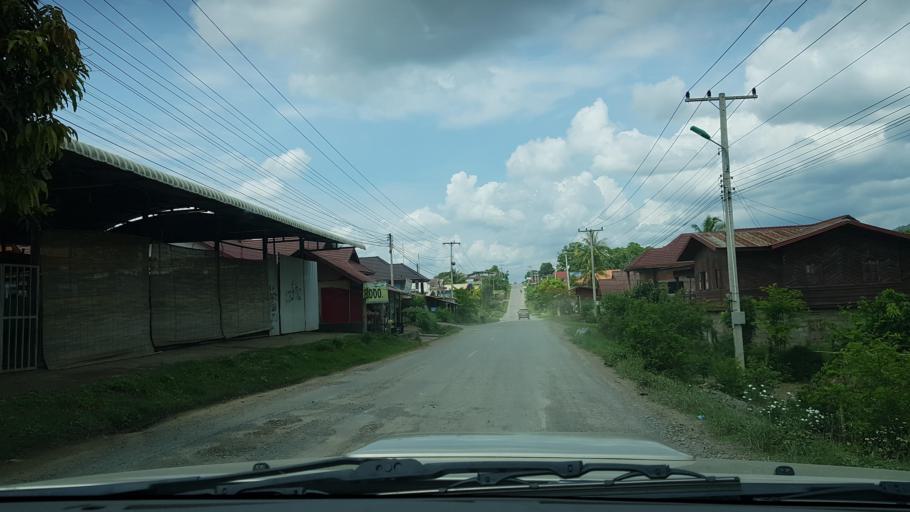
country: LA
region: Loungnamtha
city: Muang Nale
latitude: 20.1350
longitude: 101.4484
